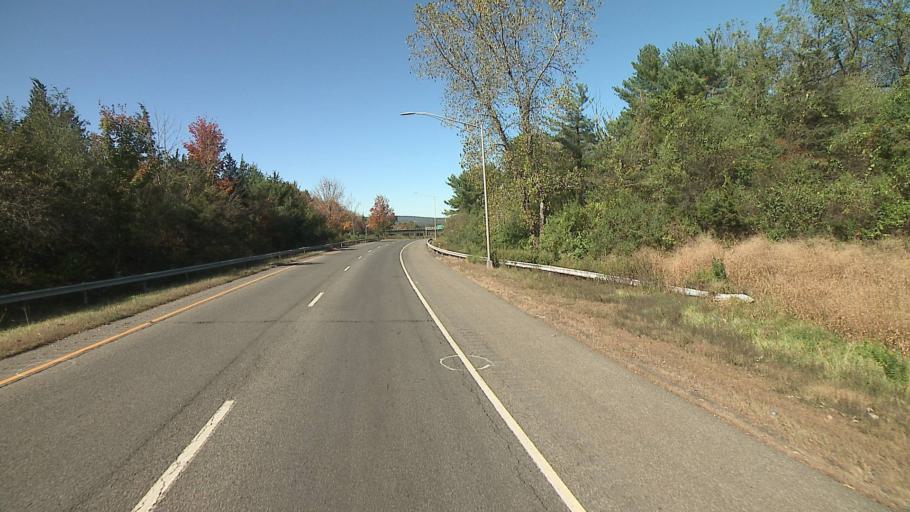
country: US
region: Connecticut
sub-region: New Haven County
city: Meriden
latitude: 41.5295
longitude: -72.7493
